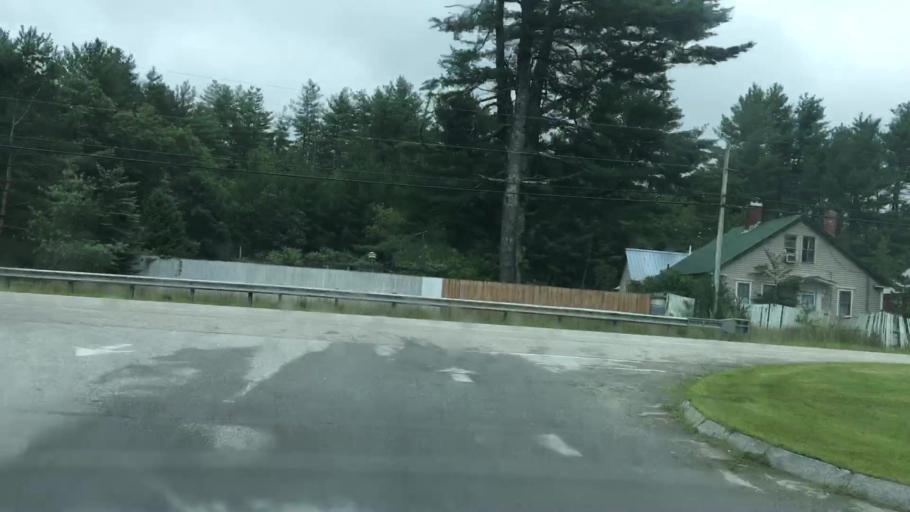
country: US
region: Maine
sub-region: Oxford County
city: Fryeburg
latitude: 44.0005
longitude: -70.9979
